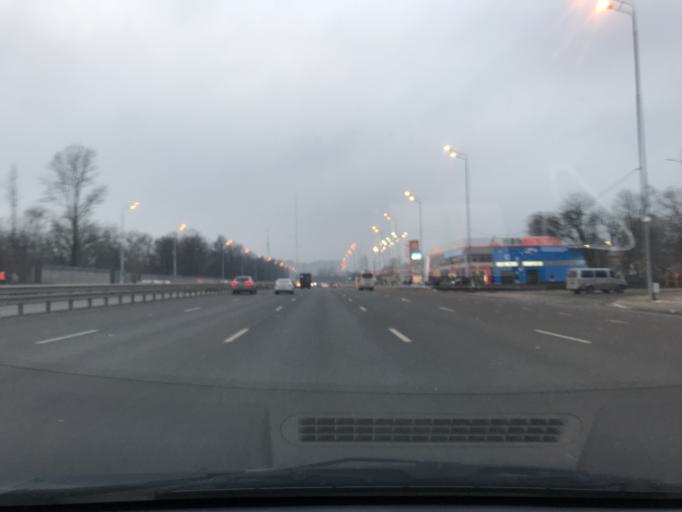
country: RU
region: Moskovskaya
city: Saltykovka
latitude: 55.7937
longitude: 37.9188
